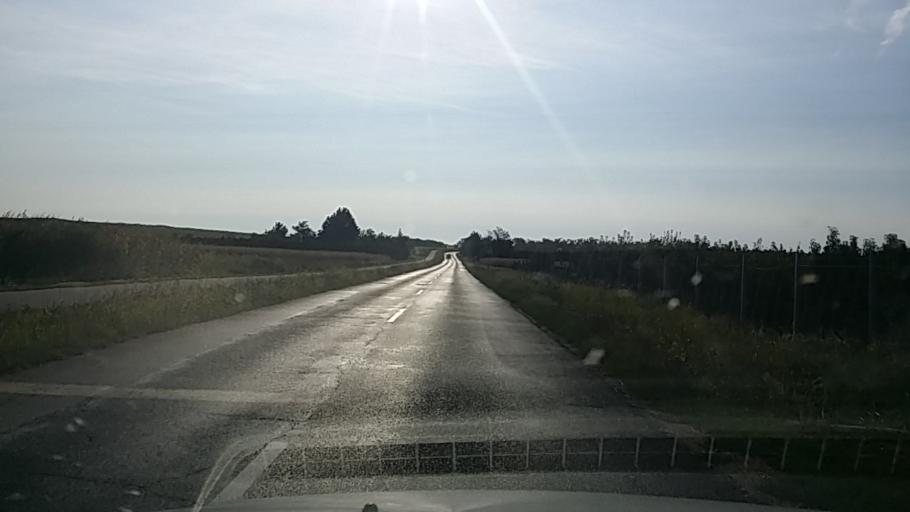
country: HU
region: Gyor-Moson-Sopron
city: Fertod
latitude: 47.6195
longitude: 16.8037
